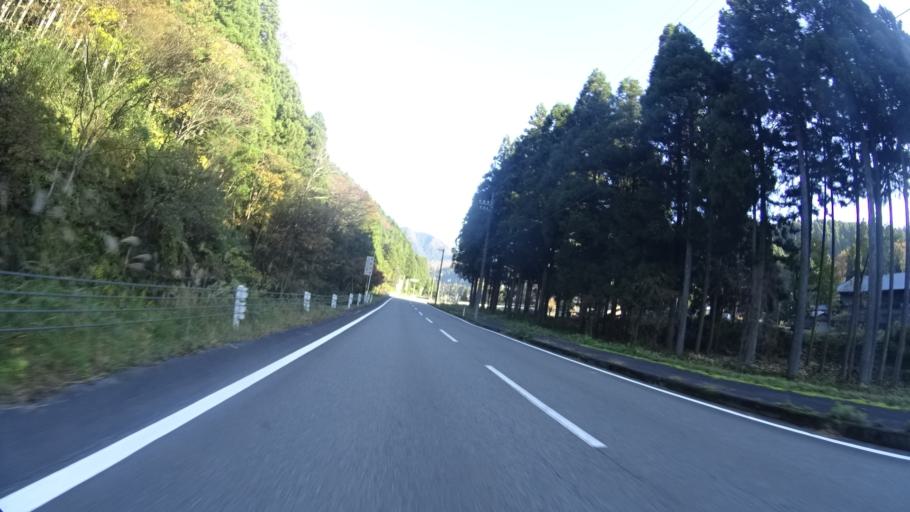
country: JP
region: Fukui
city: Maruoka
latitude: 36.1535
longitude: 136.3313
